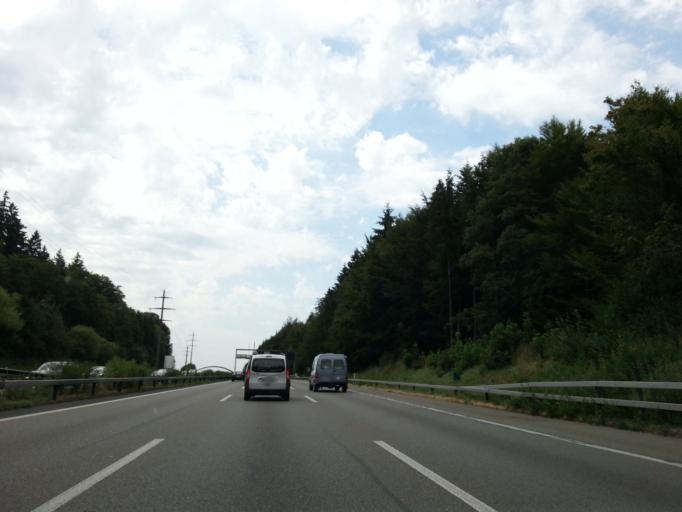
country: CH
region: Bern
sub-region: Bern-Mittelland District
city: Bolligen
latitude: 46.9982
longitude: 7.4872
